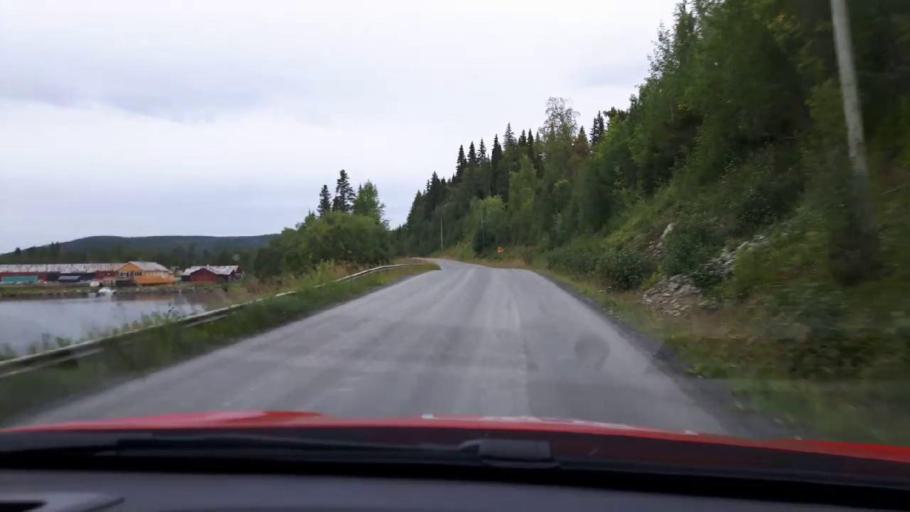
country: SE
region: Jaemtland
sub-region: Are Kommun
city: Jarpen
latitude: 63.4092
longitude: 13.3579
